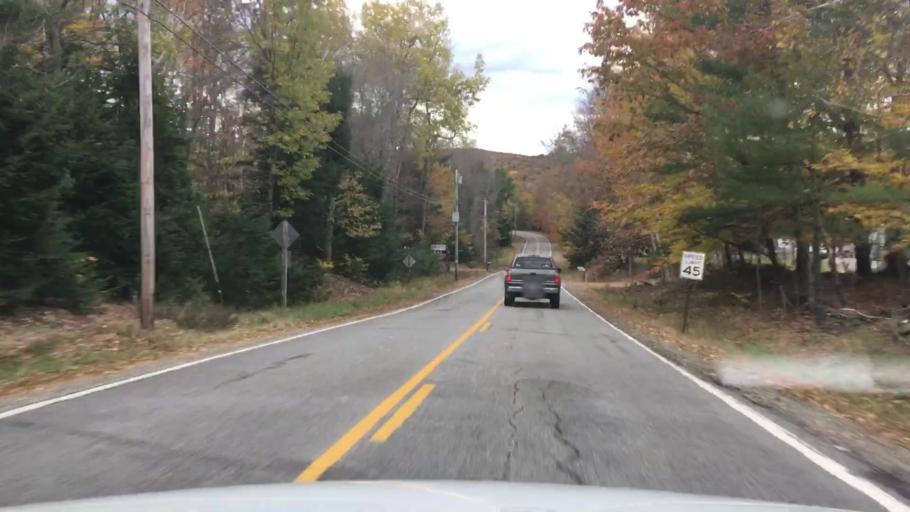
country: US
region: Maine
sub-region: Androscoggin County
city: Sabattus
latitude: 44.1354
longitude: -70.0005
